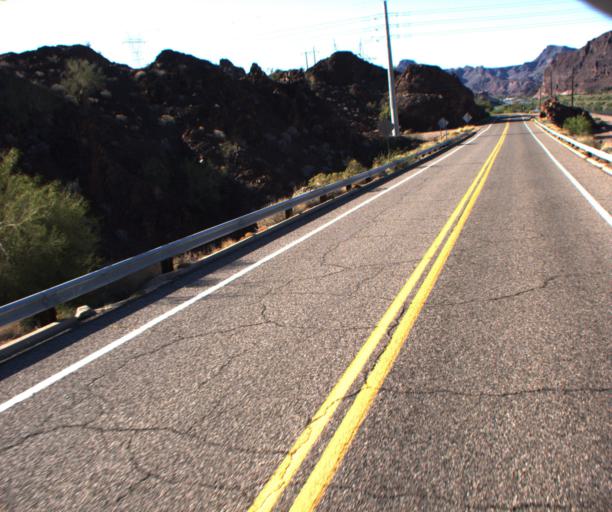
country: US
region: Arizona
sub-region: La Paz County
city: Cienega Springs
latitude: 34.2932
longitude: -114.1378
